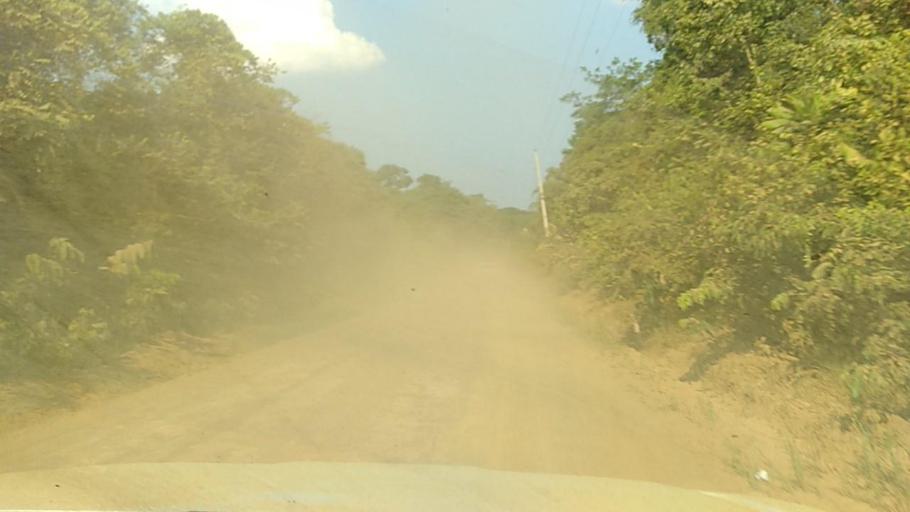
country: BR
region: Rondonia
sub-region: Porto Velho
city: Porto Velho
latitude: -8.6702
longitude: -64.0058
